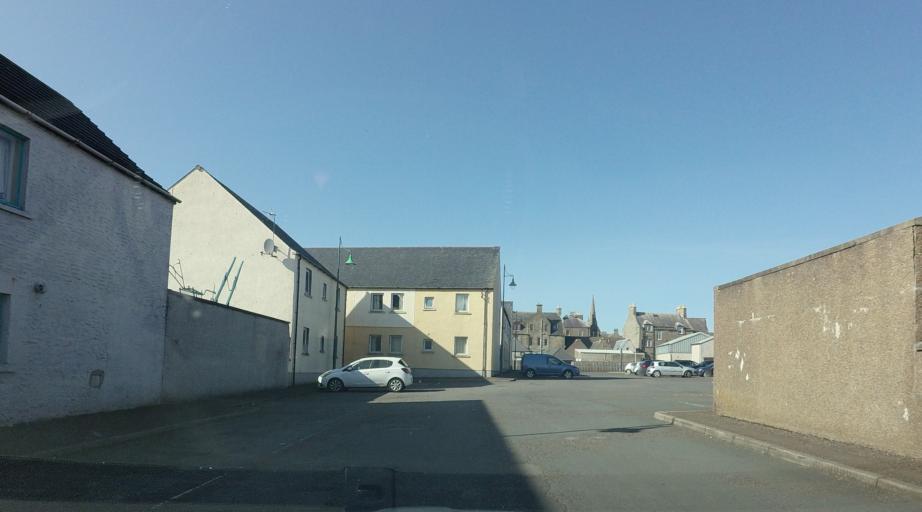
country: GB
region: Scotland
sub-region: Highland
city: Thurso
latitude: 58.5938
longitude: -3.5188
